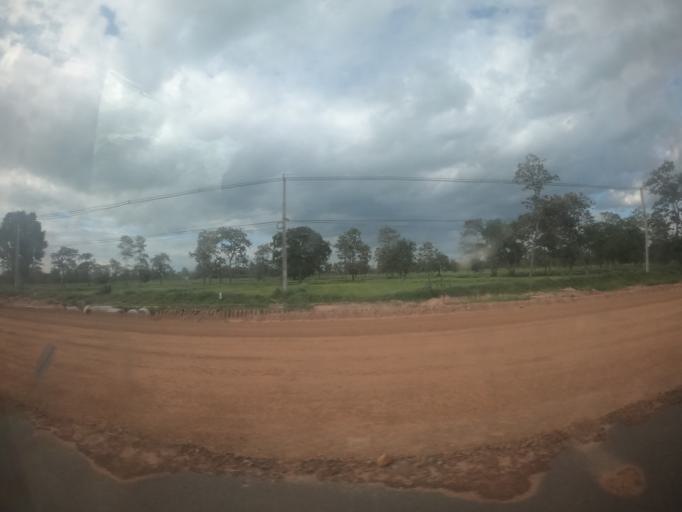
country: TH
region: Surin
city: Kap Choeng
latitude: 14.5129
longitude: 103.5502
